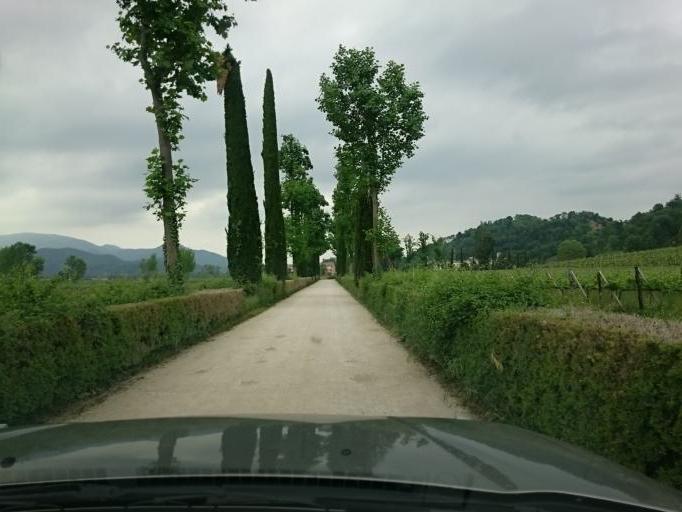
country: IT
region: Veneto
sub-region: Provincia di Padova
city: Battaglia Terme
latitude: 45.2754
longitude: 11.7652
